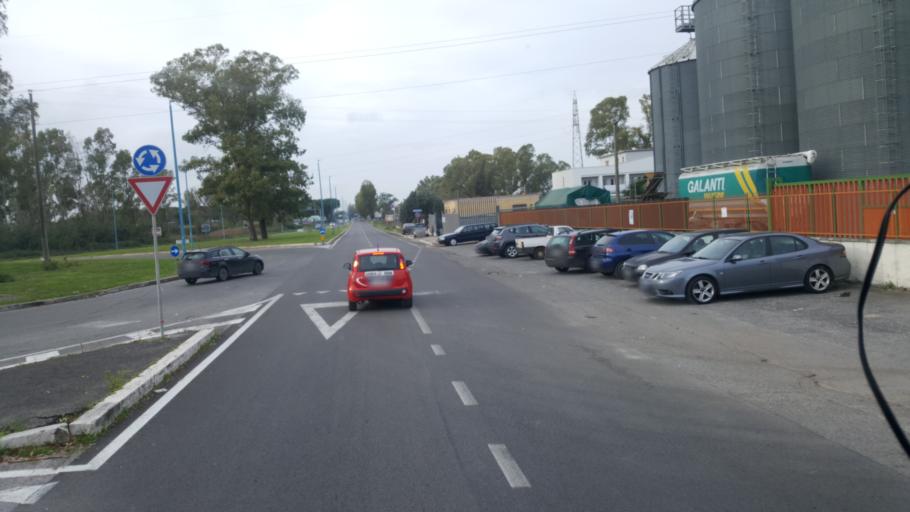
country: IT
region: Latium
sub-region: Provincia di Latina
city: Latina
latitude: 41.4776
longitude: 12.8753
